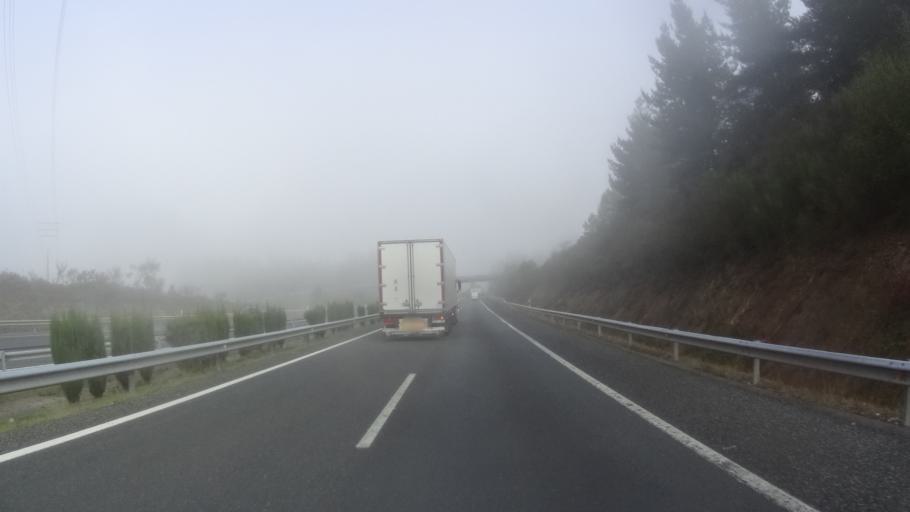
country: ES
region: Galicia
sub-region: Provincia de Lugo
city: O Paramo
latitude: 42.9250
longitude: -7.3575
